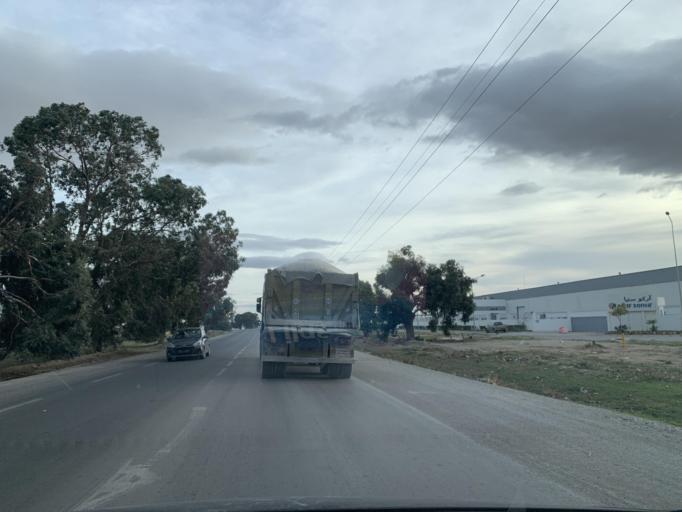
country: TN
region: Susah
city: Harqalah
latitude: 36.1094
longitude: 10.3863
